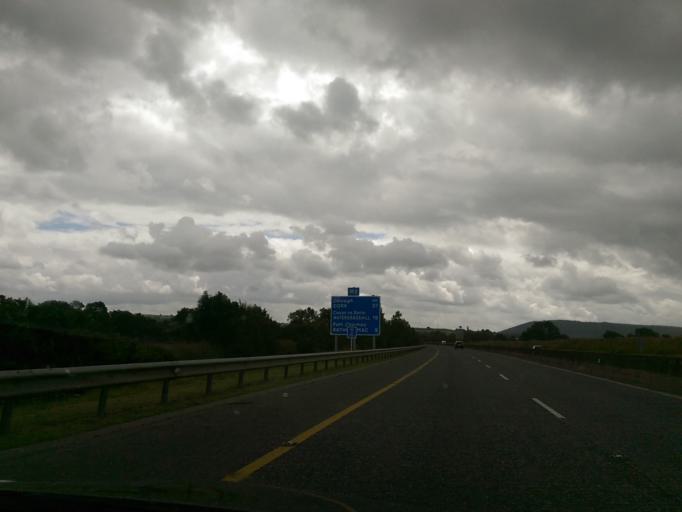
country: IE
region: Munster
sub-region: County Cork
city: Fermoy
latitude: 52.1555
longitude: -8.2660
